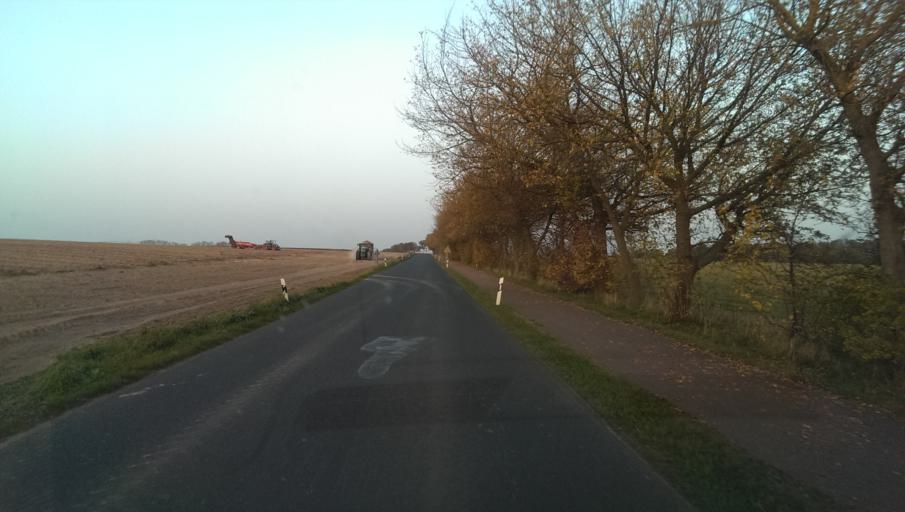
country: DE
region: Brandenburg
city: Juterbog
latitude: 51.9331
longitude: 13.0506
